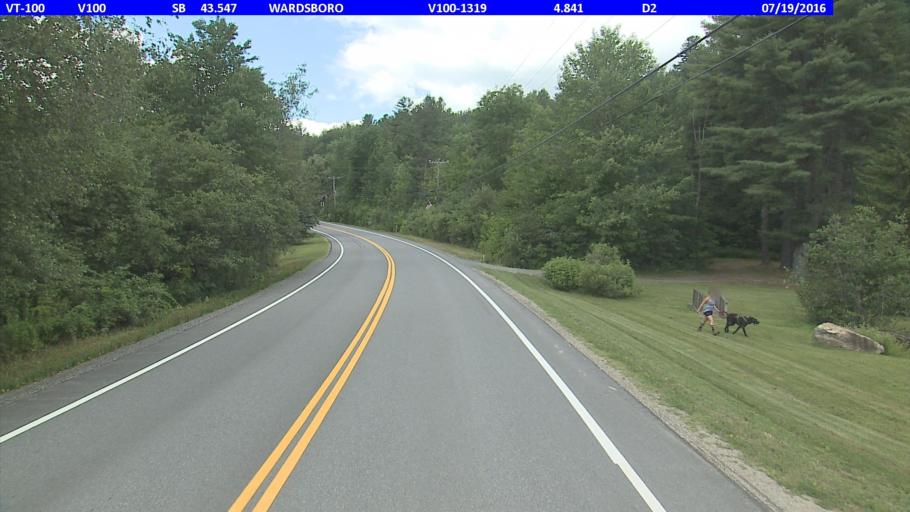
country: US
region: Vermont
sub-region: Windham County
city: Dover
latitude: 43.0680
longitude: -72.8624
